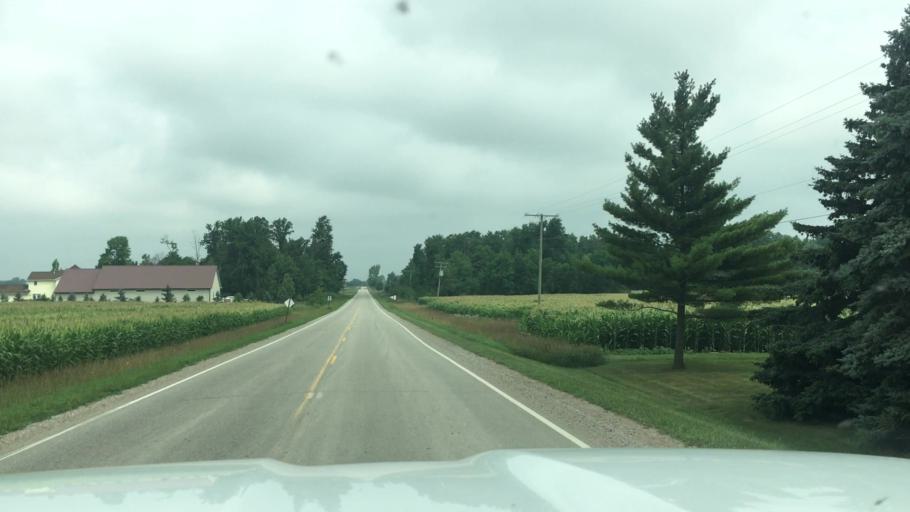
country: US
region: Michigan
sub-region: Sanilac County
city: Marlette
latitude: 43.3145
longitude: -82.9839
